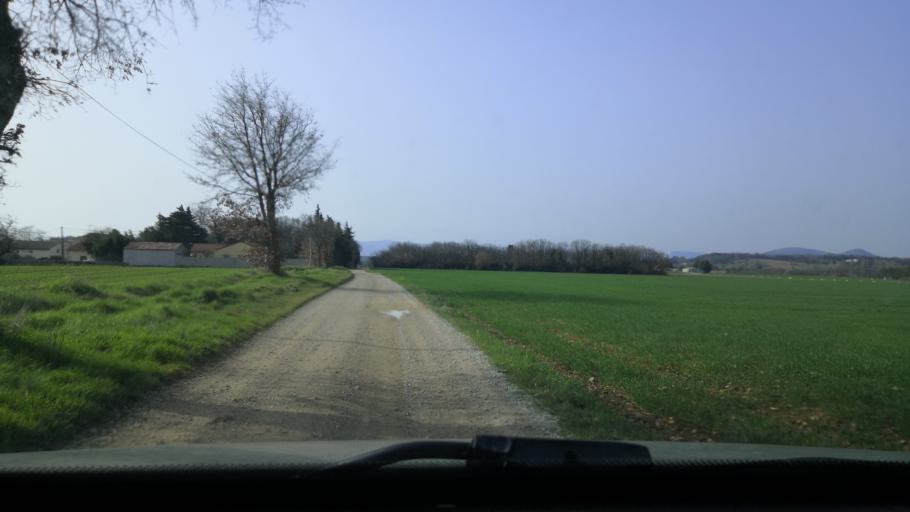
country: FR
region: Rhone-Alpes
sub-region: Departement de la Drome
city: La Begude-de-Mazenc
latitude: 44.5562
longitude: 4.8940
